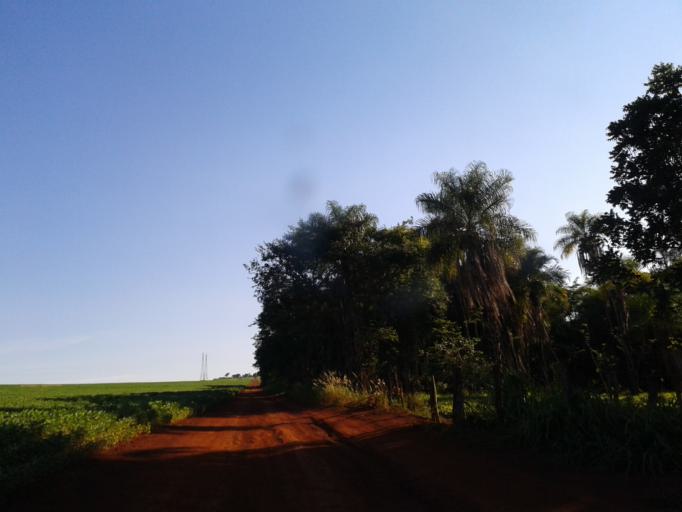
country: BR
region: Minas Gerais
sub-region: Centralina
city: Centralina
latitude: -18.6815
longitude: -49.2794
